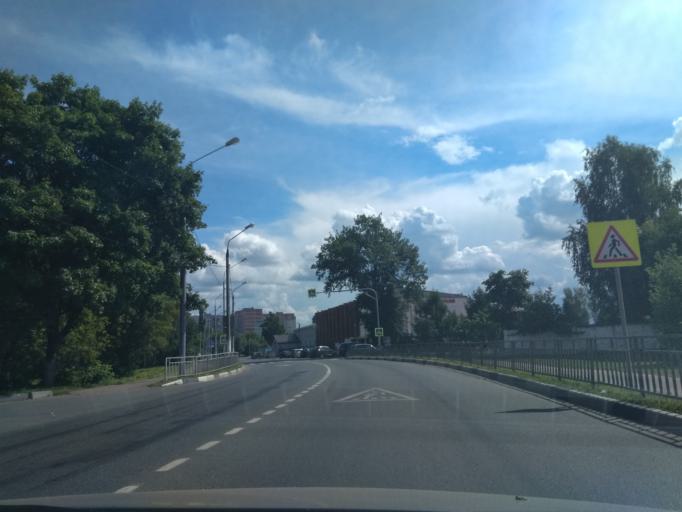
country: RU
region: Moskovskaya
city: Orekhovo-Zuyevo
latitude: 55.8016
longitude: 38.9768
